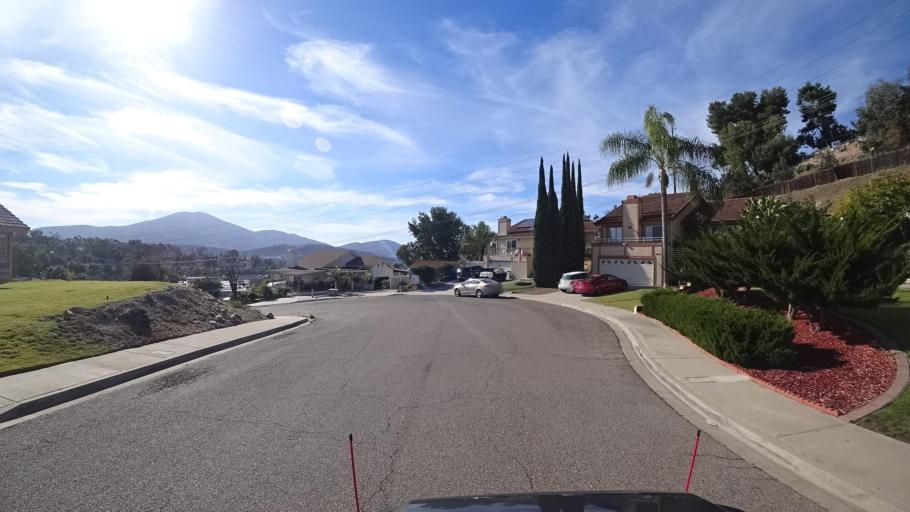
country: US
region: California
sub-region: San Diego County
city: Spring Valley
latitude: 32.7394
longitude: -116.9747
